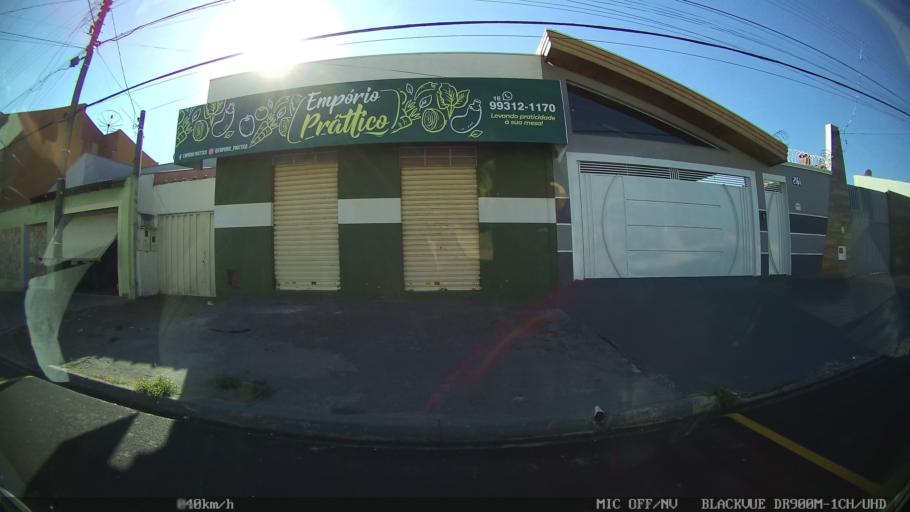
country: BR
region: Sao Paulo
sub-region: Franca
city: Franca
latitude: -20.5112
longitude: -47.4219
